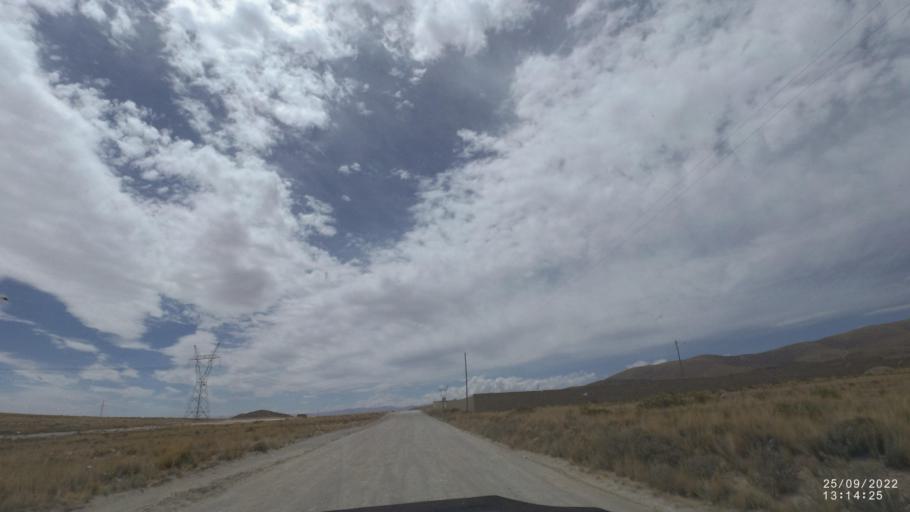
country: BO
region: Oruro
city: Oruro
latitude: -17.9382
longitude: -67.0404
